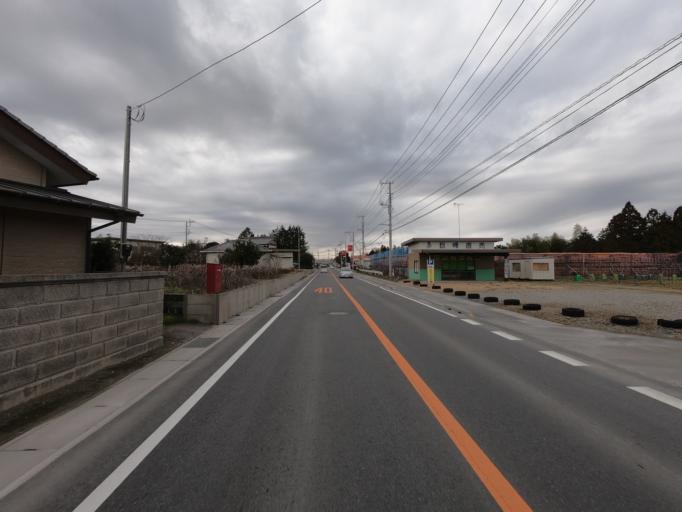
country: JP
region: Ibaraki
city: Ishioka
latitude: 36.0945
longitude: 140.3421
